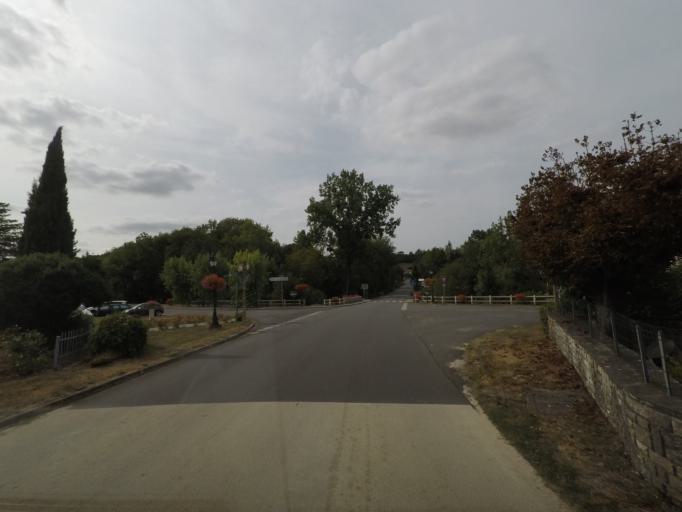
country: FR
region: Poitou-Charentes
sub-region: Departement de la Charente
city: Nanteuil-en-Vallee
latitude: 45.9987
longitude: 0.3230
